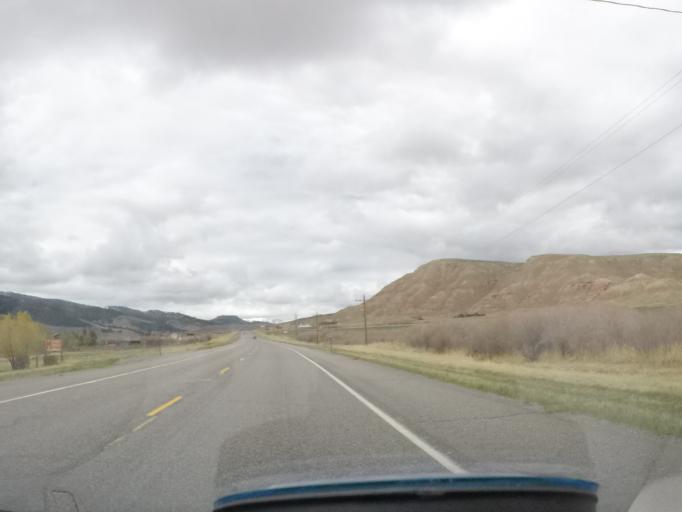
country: US
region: Wyoming
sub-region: Sublette County
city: Pinedale
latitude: 43.5678
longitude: -109.7098
